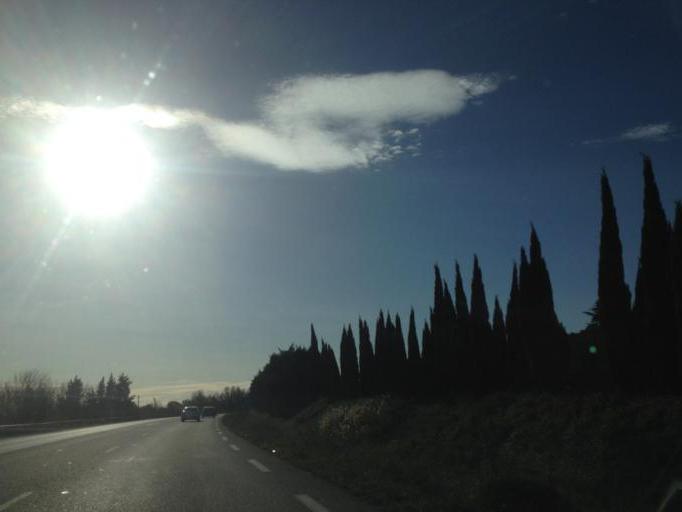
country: FR
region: Provence-Alpes-Cote d'Azur
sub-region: Departement du Vaucluse
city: Courthezon
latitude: 44.0635
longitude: 4.8873
